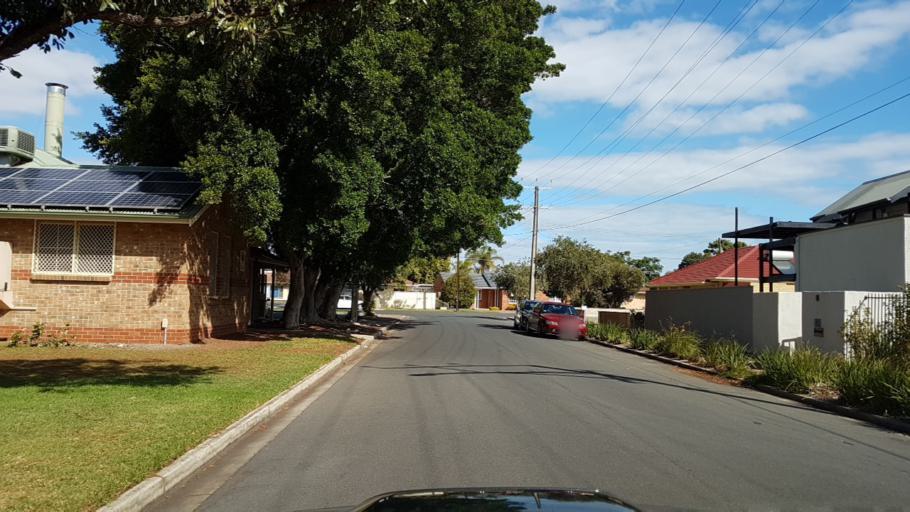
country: AU
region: South Australia
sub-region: Holdfast Bay
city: Glenelg East
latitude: -34.9732
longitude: 138.5243
